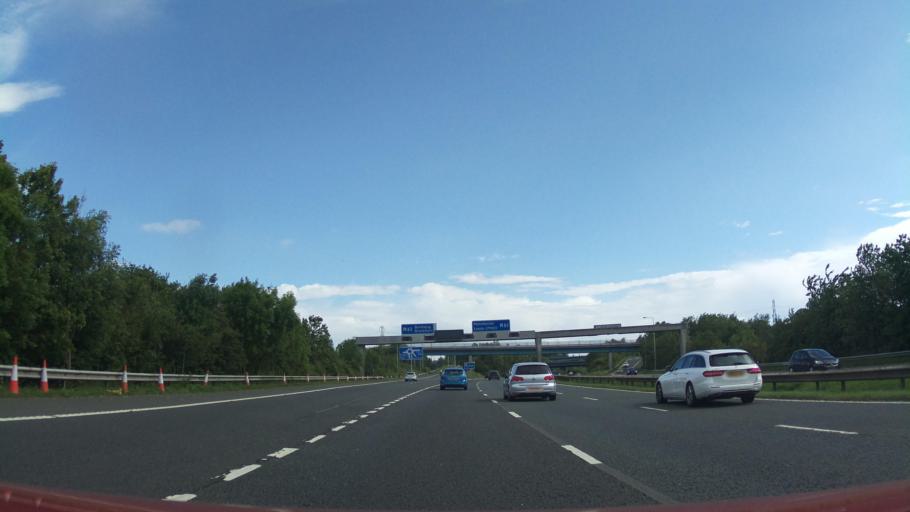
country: GB
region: England
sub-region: Lancashire
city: Clayton-le-Woods
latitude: 53.7231
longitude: -2.6311
